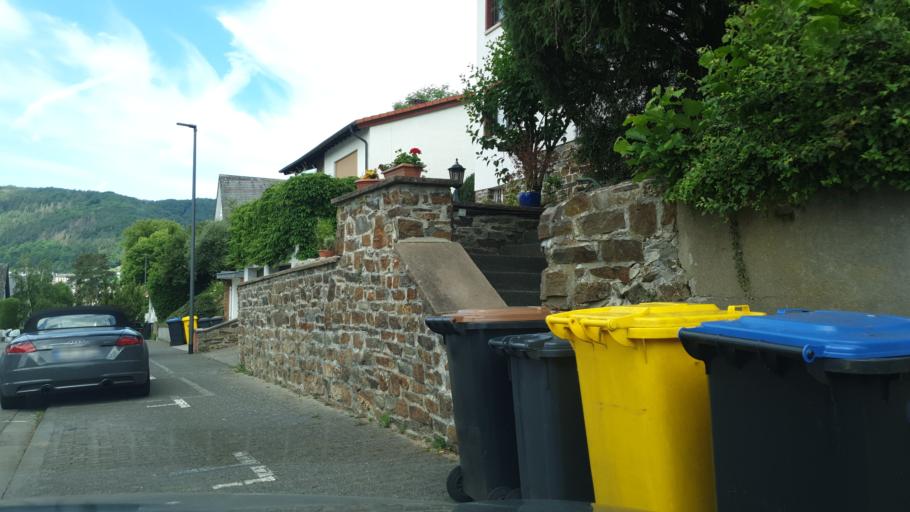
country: DE
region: Rheinland-Pfalz
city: Nassau
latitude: 50.3146
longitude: 7.8041
